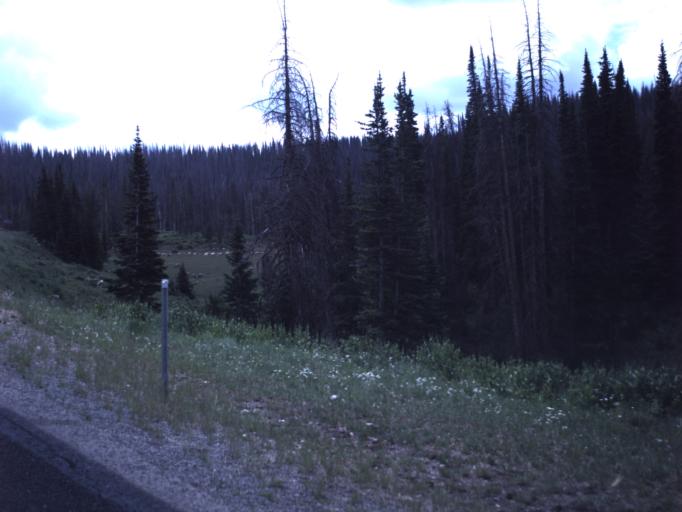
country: US
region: Utah
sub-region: Summit County
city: Francis
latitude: 40.4849
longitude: -111.0331
